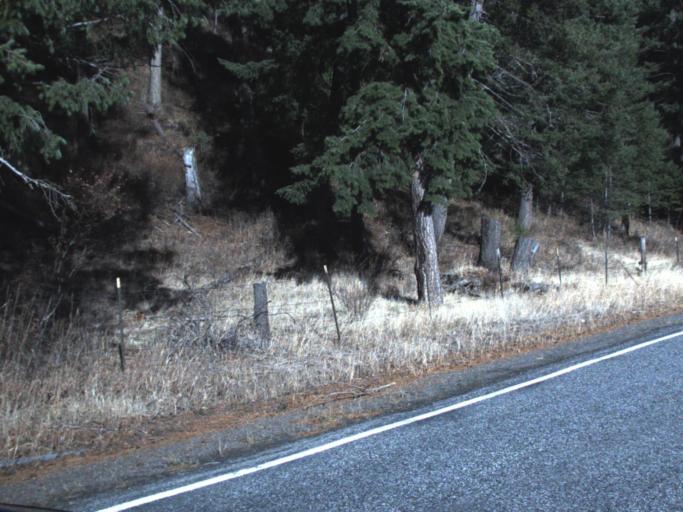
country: US
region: Washington
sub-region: Ferry County
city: Republic
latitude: 48.5792
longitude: -118.7428
